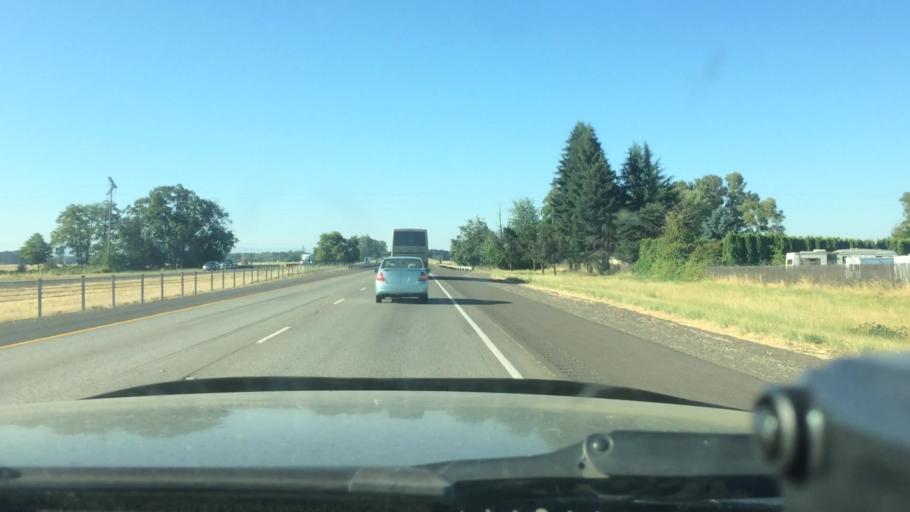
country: US
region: Oregon
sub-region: Linn County
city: Albany
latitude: 44.6073
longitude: -123.0633
